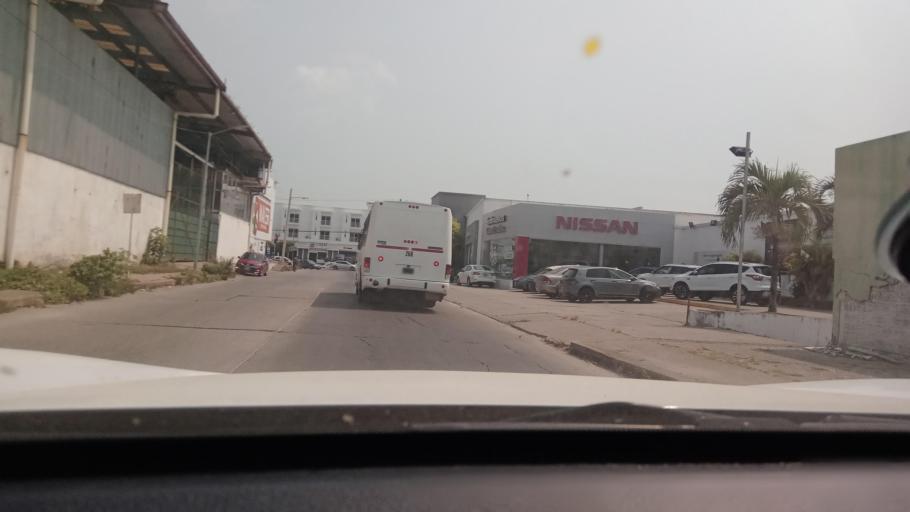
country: MX
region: Veracruz
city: Minatitlan
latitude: 17.9899
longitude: -94.5685
